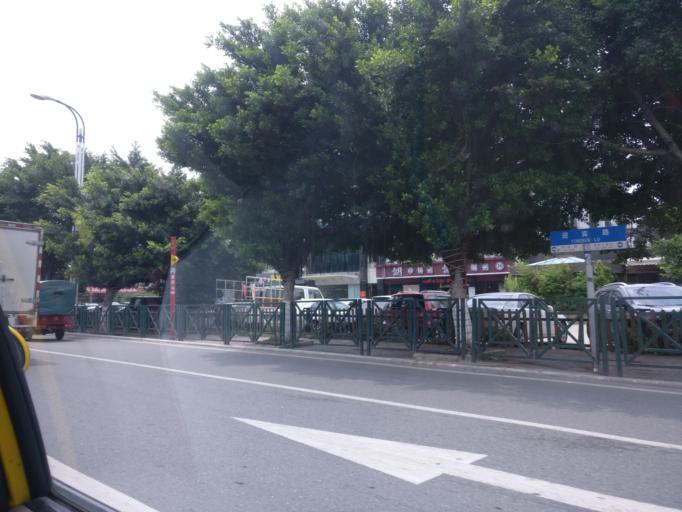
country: CN
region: Guangdong
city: Dashi
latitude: 23.0388
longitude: 113.3108
